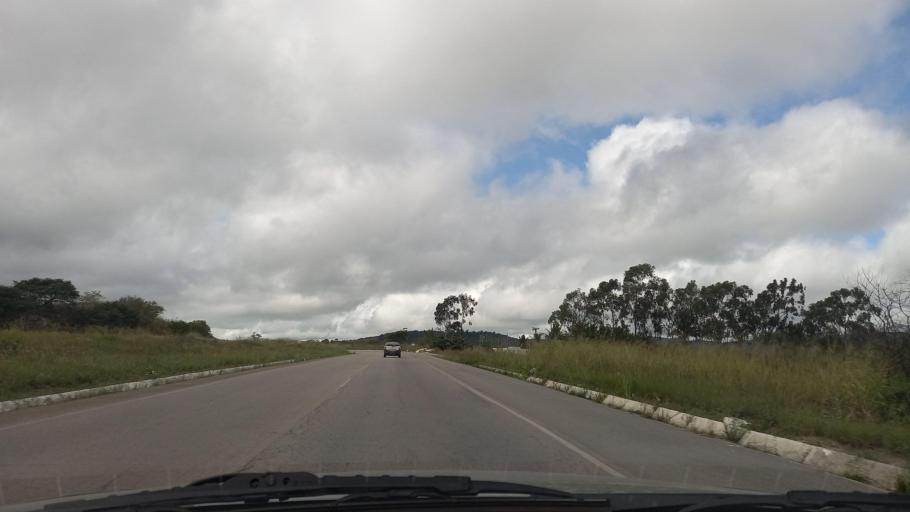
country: BR
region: Pernambuco
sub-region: Caruaru
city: Caruaru
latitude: -8.3192
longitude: -35.9914
